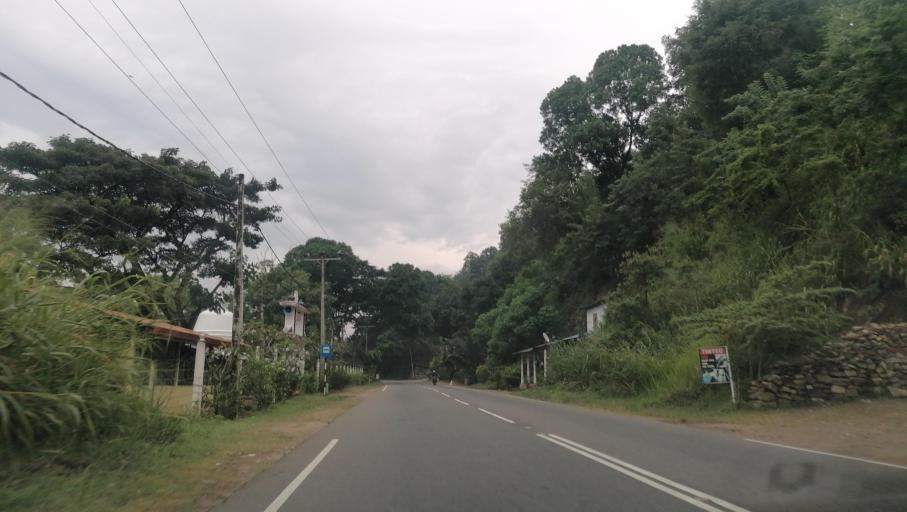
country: LK
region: Central
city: Kandy
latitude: 7.2462
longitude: 80.7241
